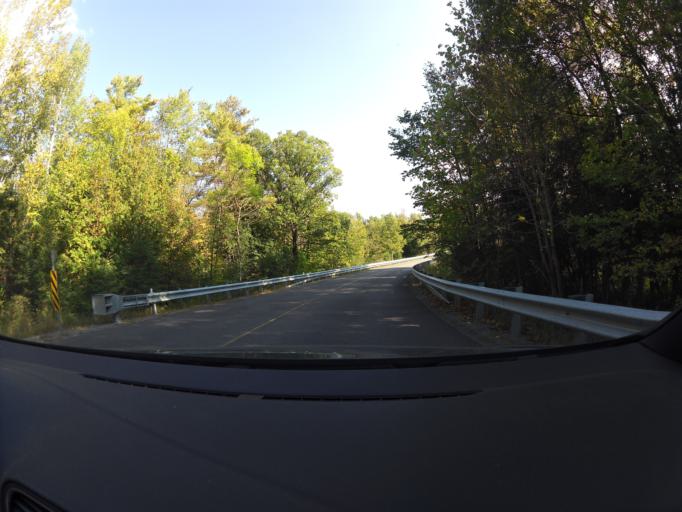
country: CA
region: Ontario
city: Arnprior
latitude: 45.4408
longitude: -76.2484
